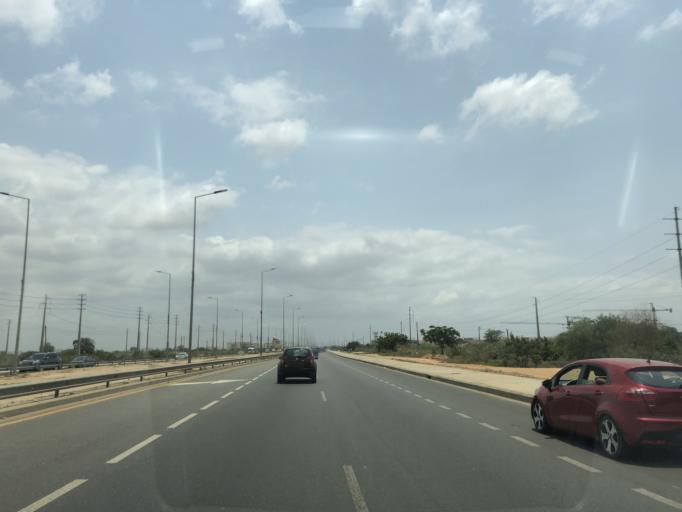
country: AO
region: Luanda
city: Luanda
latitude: -8.9493
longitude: 13.2593
